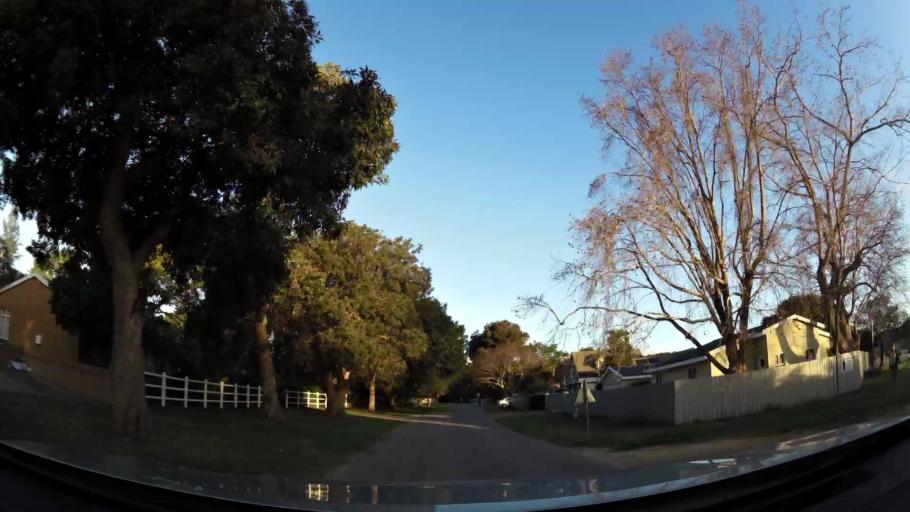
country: ZA
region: Western Cape
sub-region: Eden District Municipality
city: Knysna
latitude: -34.0174
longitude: 22.8034
